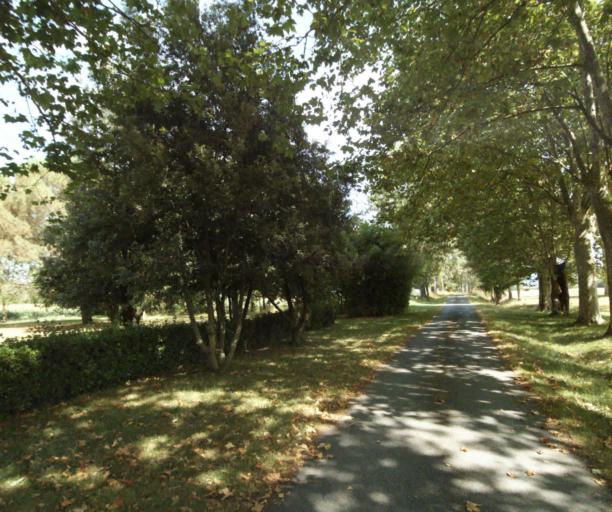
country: FR
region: Midi-Pyrenees
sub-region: Departement du Tarn
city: Soreze
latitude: 43.5078
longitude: 2.0501
